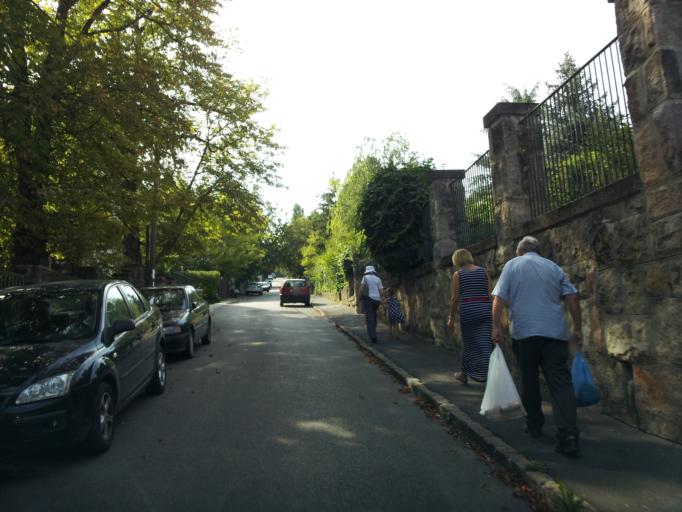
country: HU
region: Budapest
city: Budapest II. keruelet
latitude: 47.5194
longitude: 19.0284
